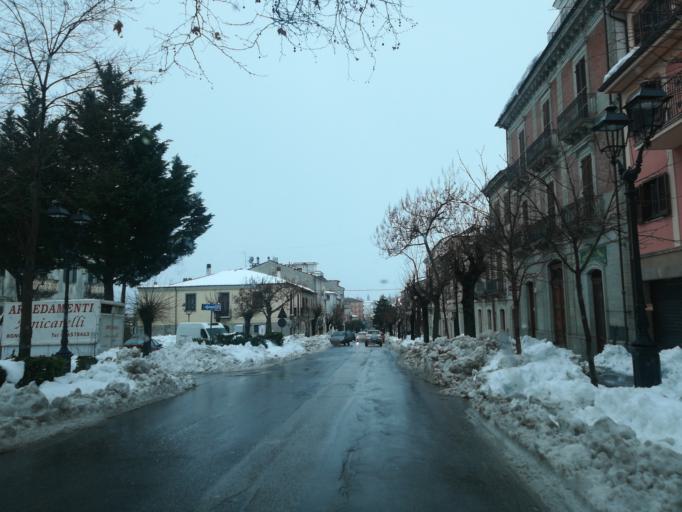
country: IT
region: Molise
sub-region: Provincia di Isernia
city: Agnone
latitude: 41.8095
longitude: 14.3762
